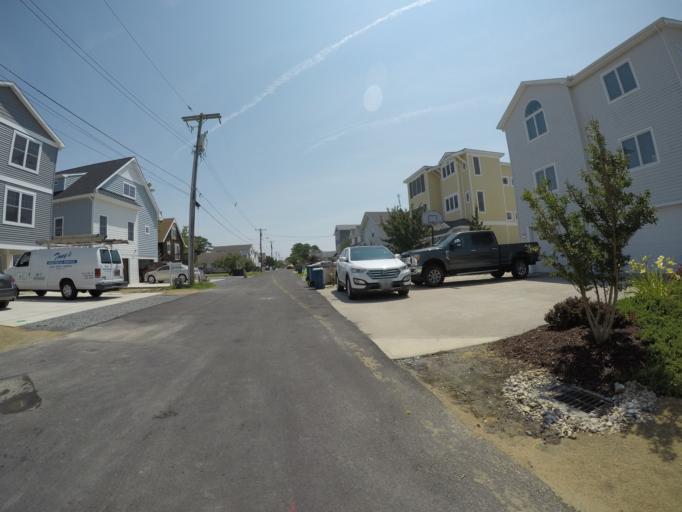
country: US
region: Delaware
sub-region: Sussex County
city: Bethany Beach
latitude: 38.5143
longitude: -75.0606
